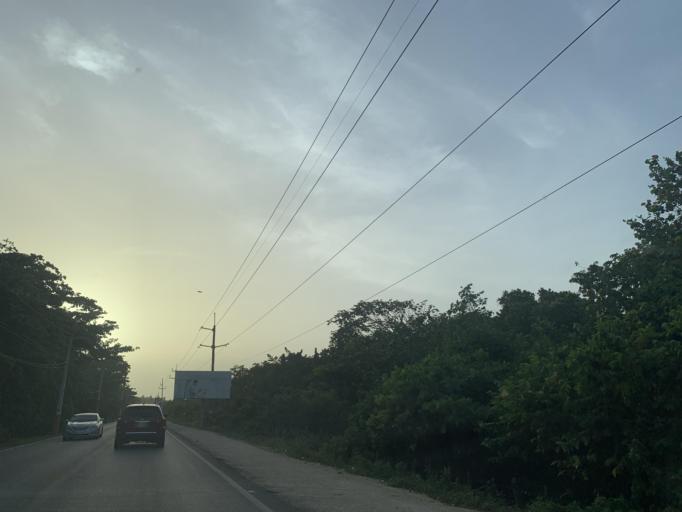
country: DO
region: Puerto Plata
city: Cabarete
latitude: 19.7697
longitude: -70.4354
